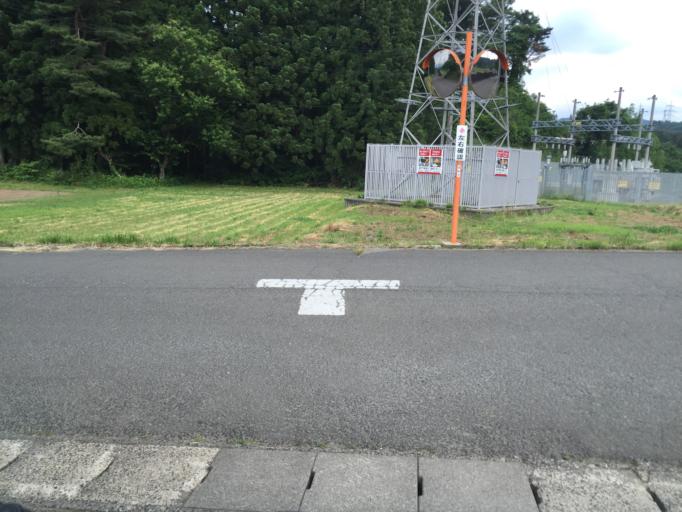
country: JP
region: Fukushima
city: Fukushima-shi
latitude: 37.7060
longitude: 140.3476
